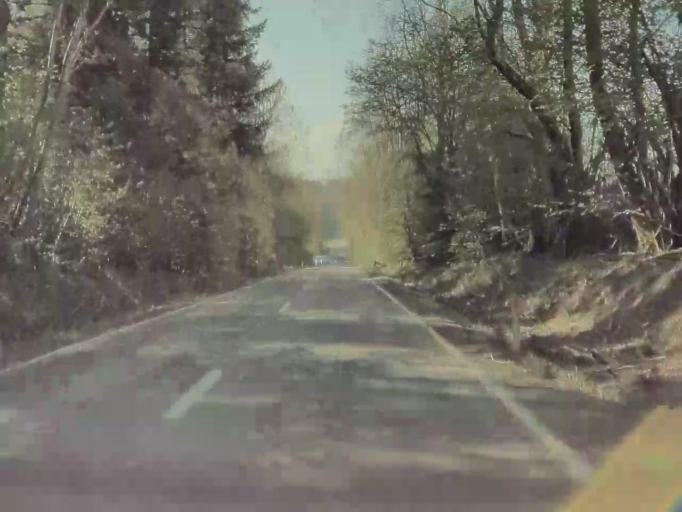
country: BE
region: Wallonia
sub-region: Province du Luxembourg
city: Tellin
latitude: 50.0344
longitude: 5.2074
